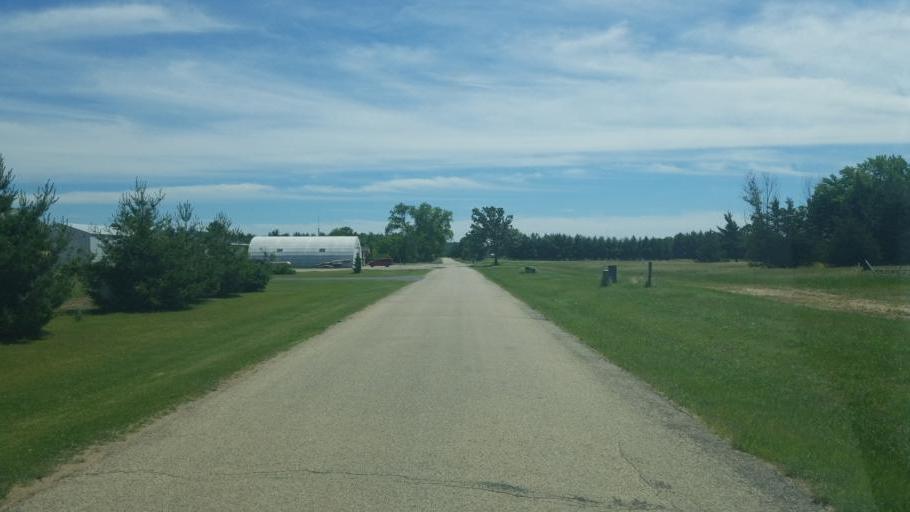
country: US
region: Wisconsin
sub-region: Adams County
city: Adams
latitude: 43.8765
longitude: -89.9406
